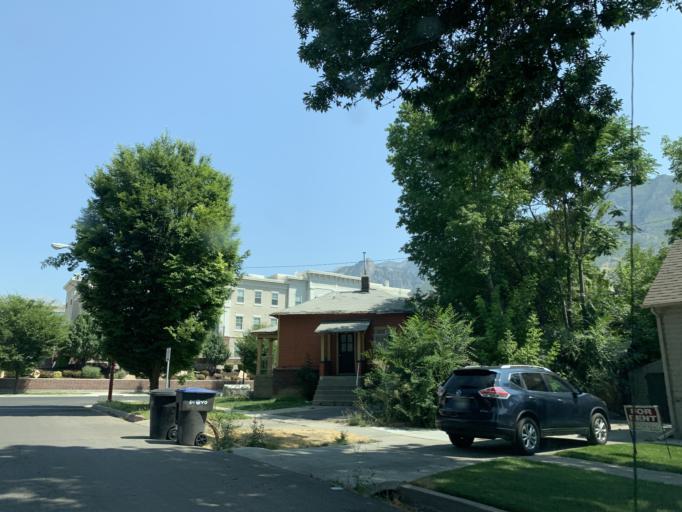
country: US
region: Utah
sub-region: Utah County
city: Provo
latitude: 40.2401
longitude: -111.6482
